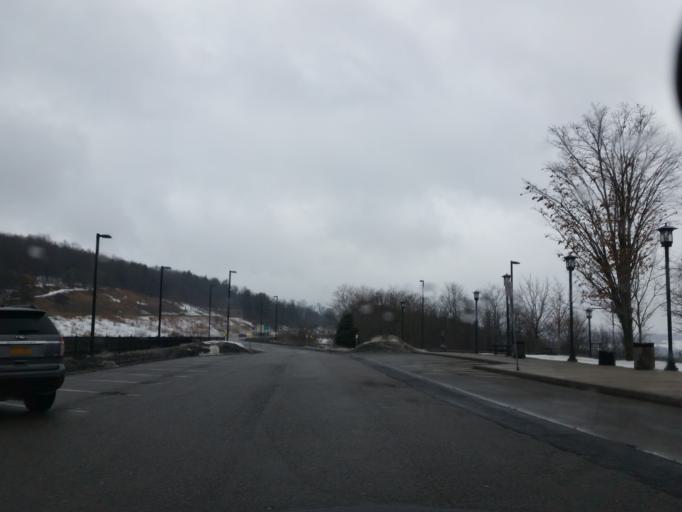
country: US
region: New York
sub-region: Chenango County
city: Lakeview
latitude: 42.3747
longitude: -75.9948
